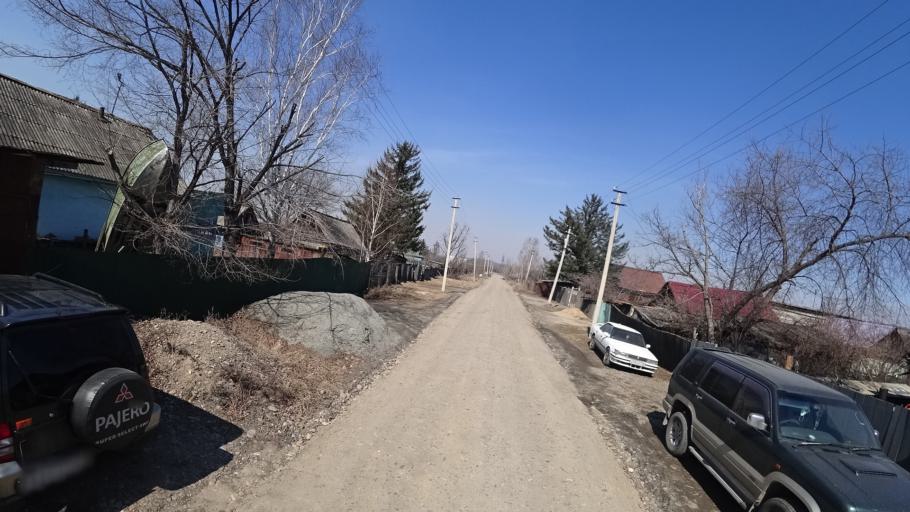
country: RU
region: Amur
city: Novobureyskiy
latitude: 49.7890
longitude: 129.8539
